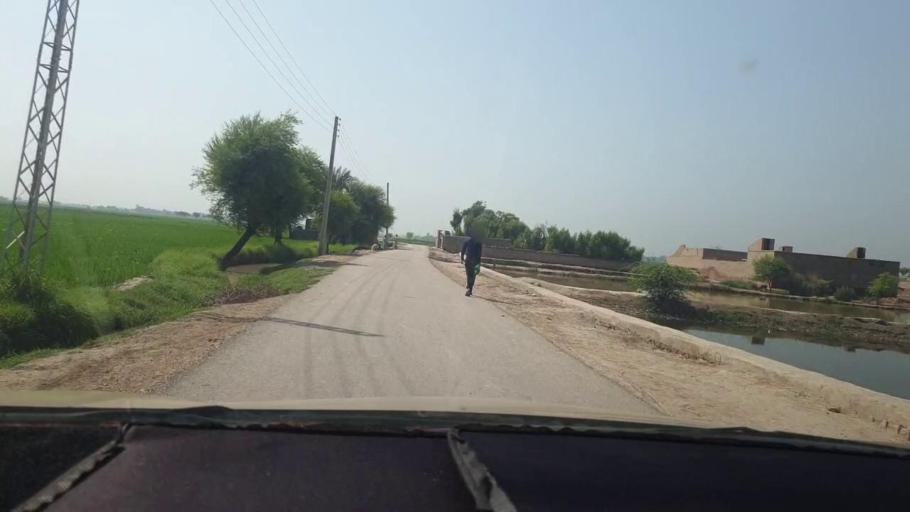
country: PK
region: Sindh
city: Kambar
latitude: 27.5694
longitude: 68.0441
